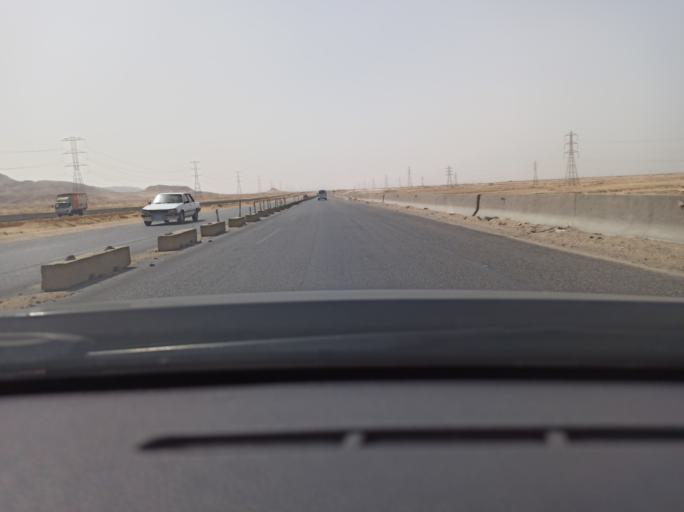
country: EG
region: Muhafazat Bani Suwayf
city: Bush
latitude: 29.1278
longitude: 31.2234
